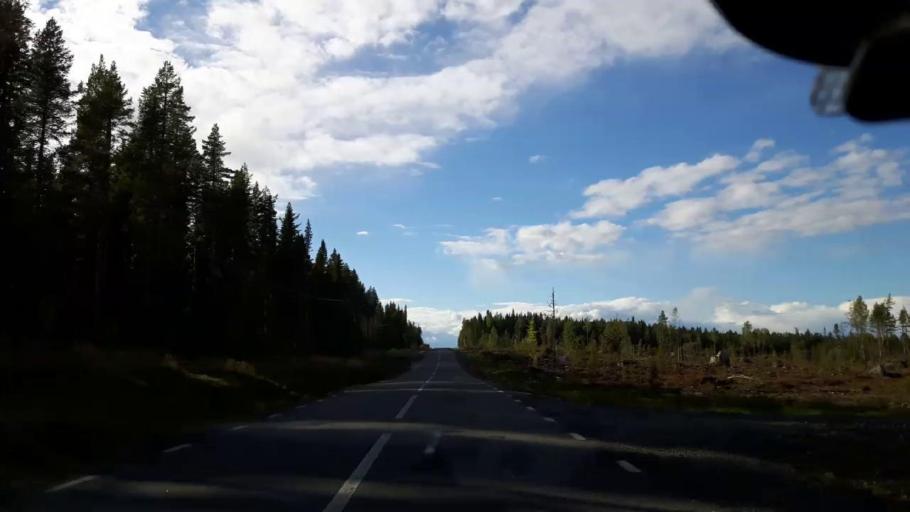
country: SE
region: Jaemtland
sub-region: Stroemsunds Kommun
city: Stroemsund
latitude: 63.5660
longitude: 15.7872
